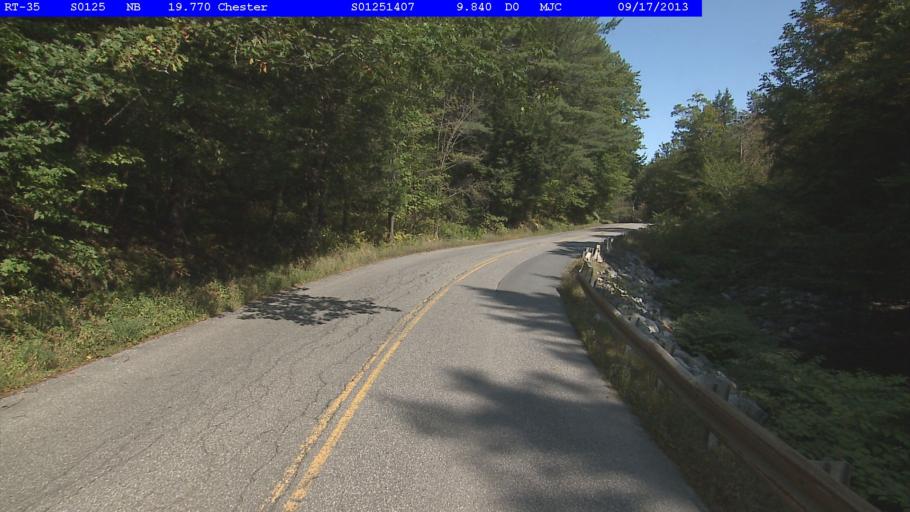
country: US
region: Vermont
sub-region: Windsor County
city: Chester
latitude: 43.2453
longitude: -72.6045
